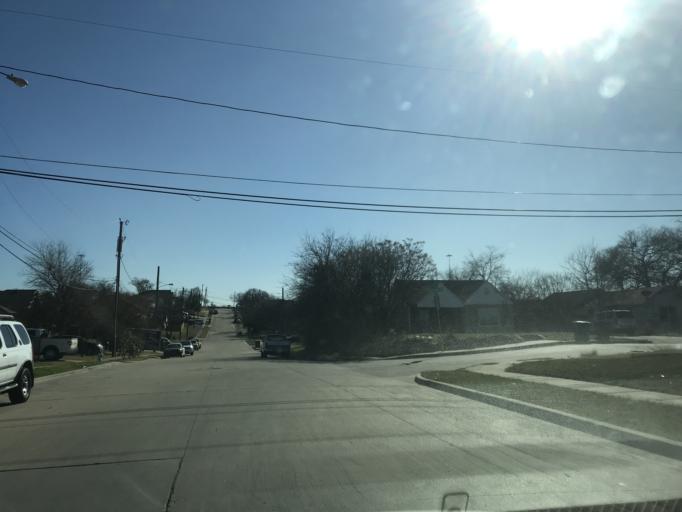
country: US
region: Texas
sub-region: Dallas County
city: Cockrell Hill
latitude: 32.7697
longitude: -96.9056
